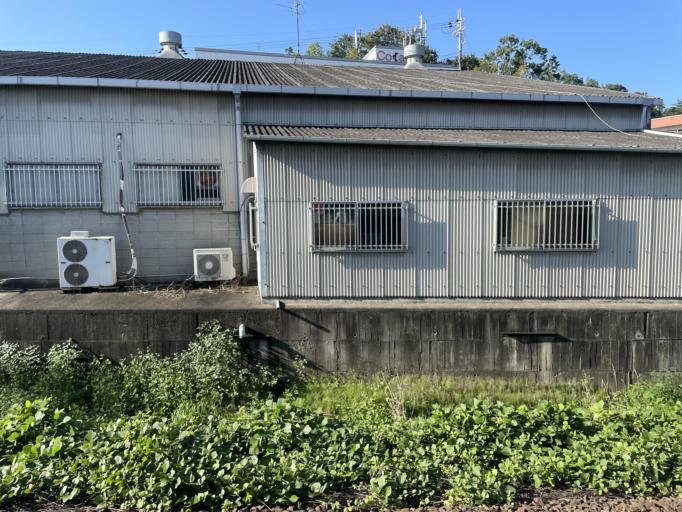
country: JP
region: Nara
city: Kashihara-shi
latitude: 34.5271
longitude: 135.7315
